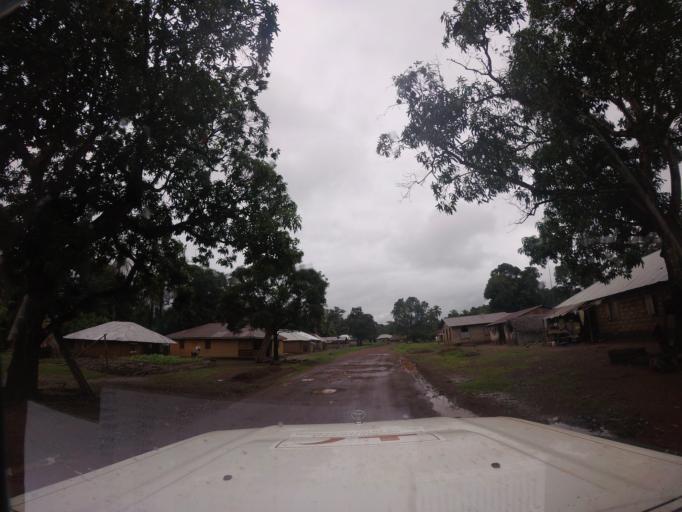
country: SL
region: Northern Province
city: Kambia
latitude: 9.1443
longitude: -12.8817
